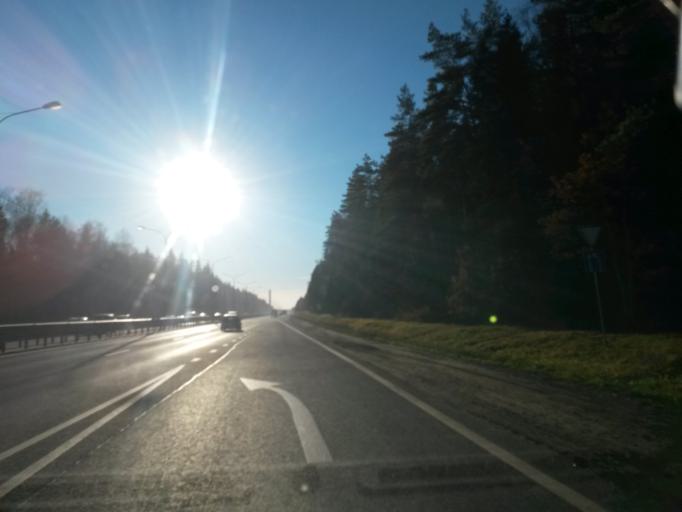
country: RU
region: Moskovskaya
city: Zelenogradskiy
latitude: 56.1041
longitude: 37.9554
